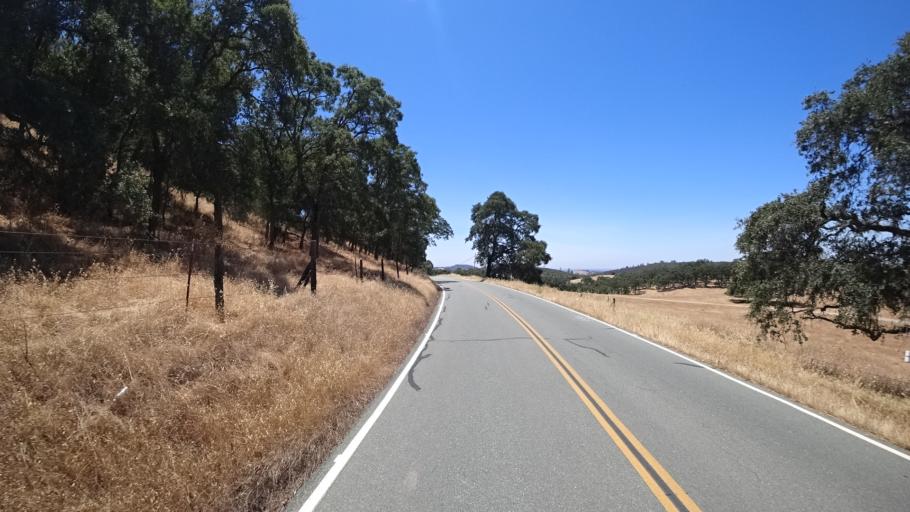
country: US
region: California
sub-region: Calaveras County
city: Valley Springs
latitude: 38.2457
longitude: -120.7823
